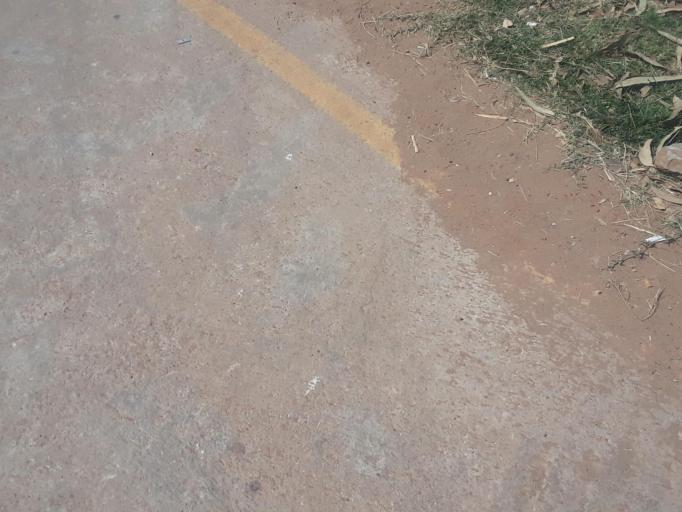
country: ZM
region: Lusaka
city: Lusaka
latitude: -15.3582
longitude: 28.2826
